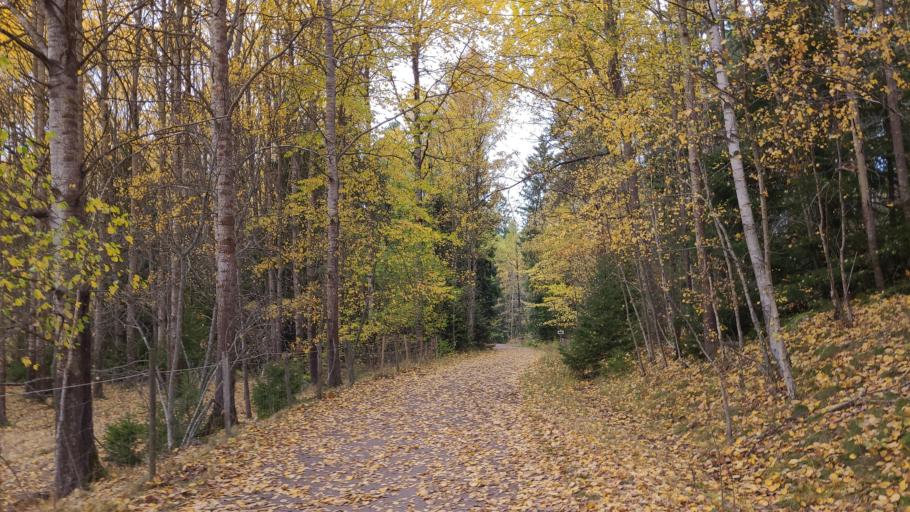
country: SE
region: Stockholm
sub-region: Solna Kommun
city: Rasunda
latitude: 59.3894
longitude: 17.9762
